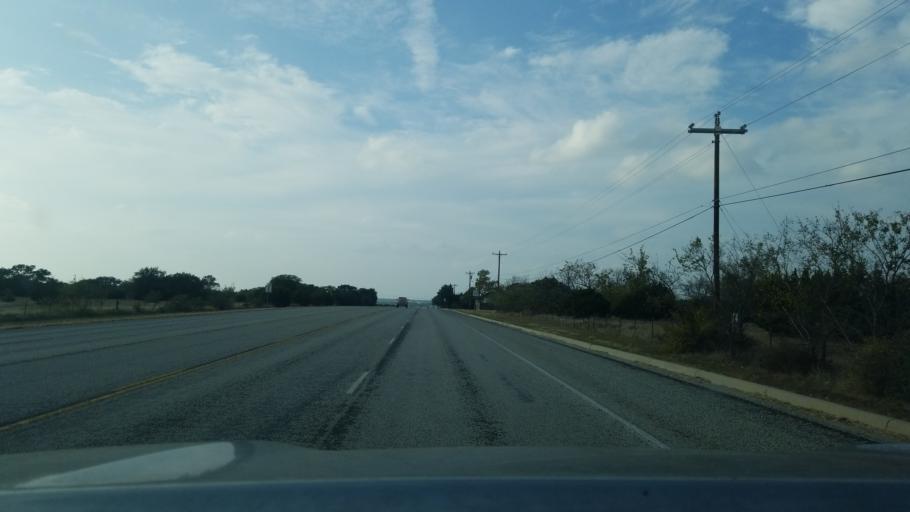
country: US
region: Texas
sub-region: Lampasas County
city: Lampasas
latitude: 31.2233
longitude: -98.3993
